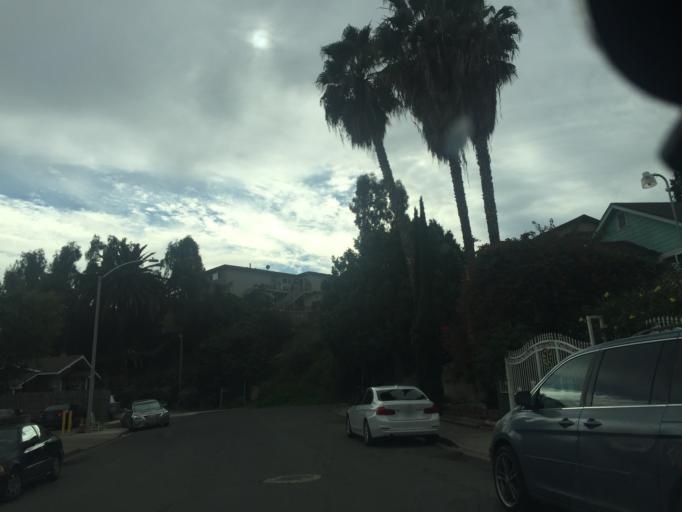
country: US
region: California
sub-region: San Diego County
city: Lemon Grove
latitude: 32.7520
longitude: -117.0869
